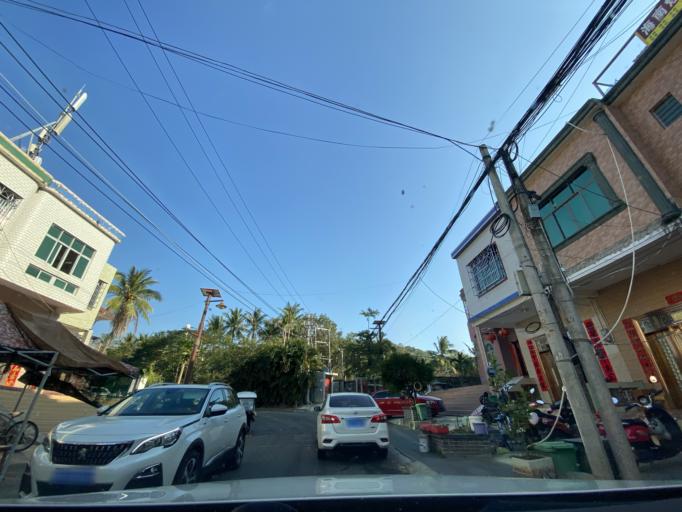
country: CN
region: Hainan
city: Yingzhou
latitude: 18.3871
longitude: 109.8197
